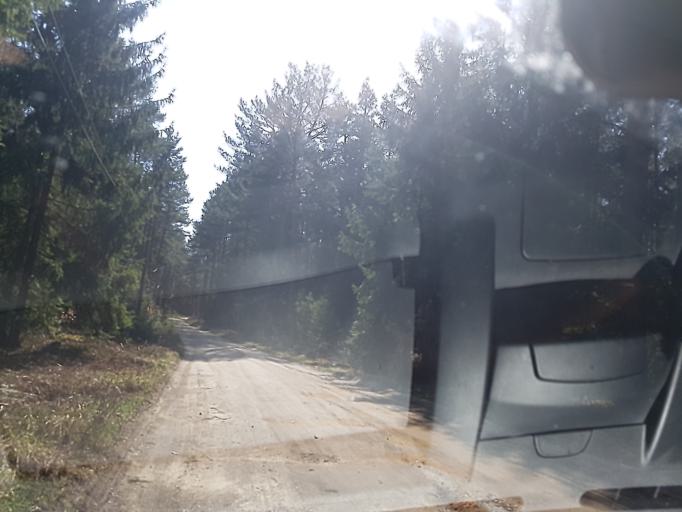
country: DE
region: Brandenburg
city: Schonborn
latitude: 51.5767
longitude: 13.4832
